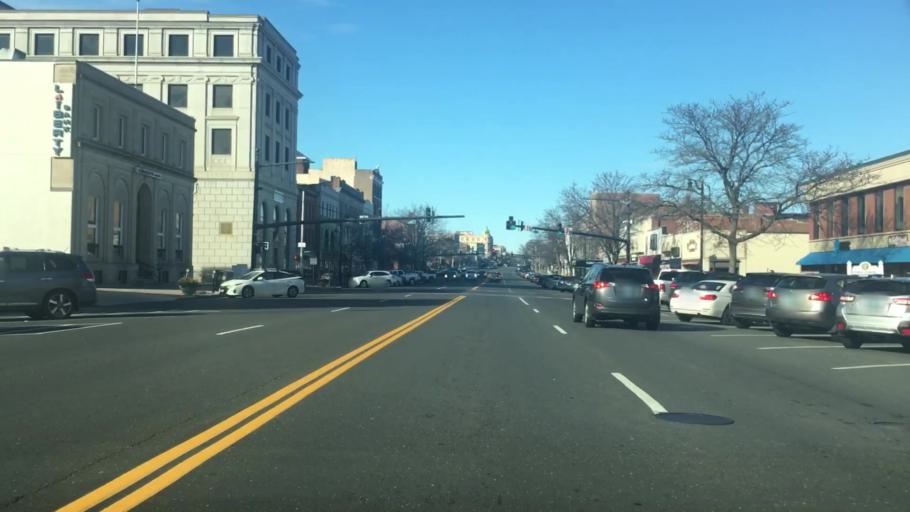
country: US
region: Connecticut
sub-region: Middlesex County
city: Middletown
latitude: 41.5599
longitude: -72.6494
